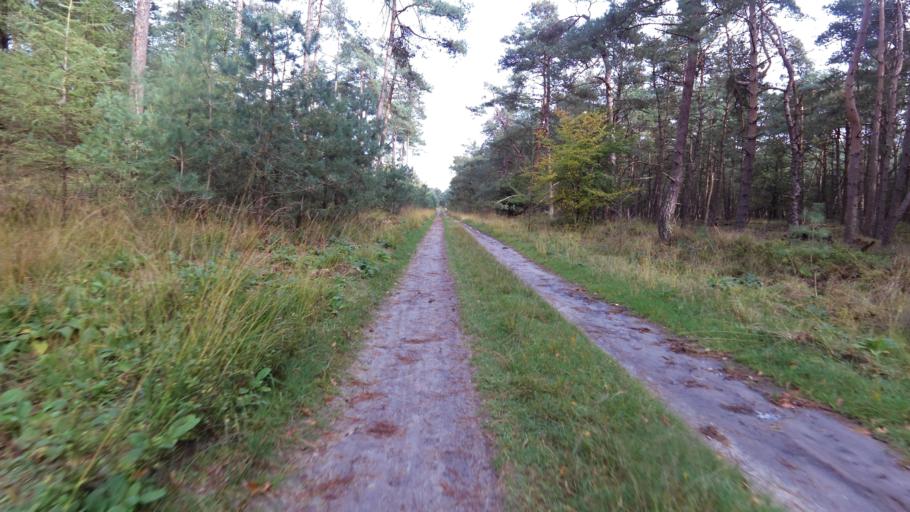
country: NL
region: Gelderland
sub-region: Gemeente Apeldoorn
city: Uddel
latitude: 52.3116
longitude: 5.8546
